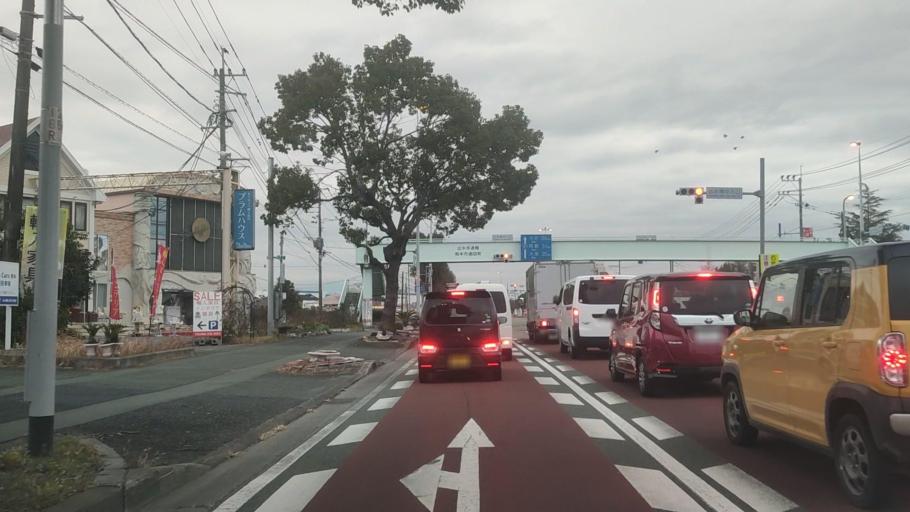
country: JP
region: Kumamoto
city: Kumamoto
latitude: 32.7708
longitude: 130.7297
